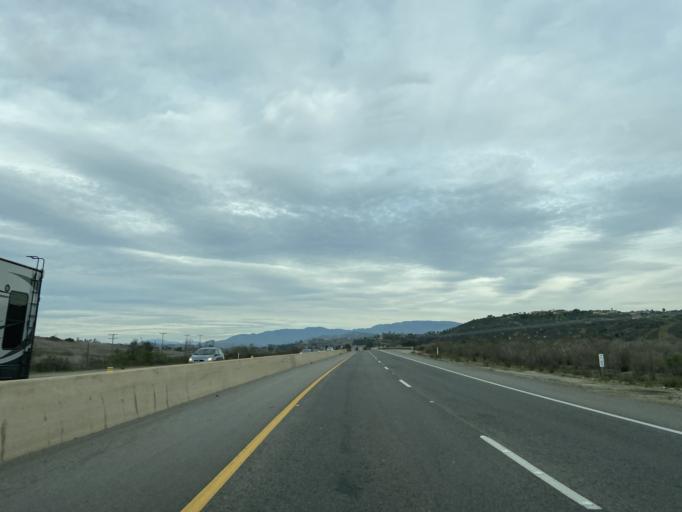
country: US
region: California
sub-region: San Diego County
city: Bonsall
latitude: 33.2771
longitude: -117.2314
